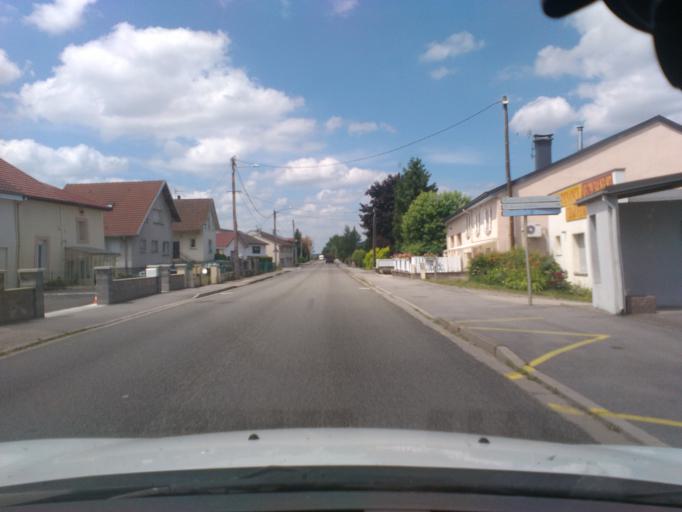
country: FR
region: Lorraine
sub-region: Departement des Vosges
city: Deyvillers
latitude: 48.1997
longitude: 6.5143
